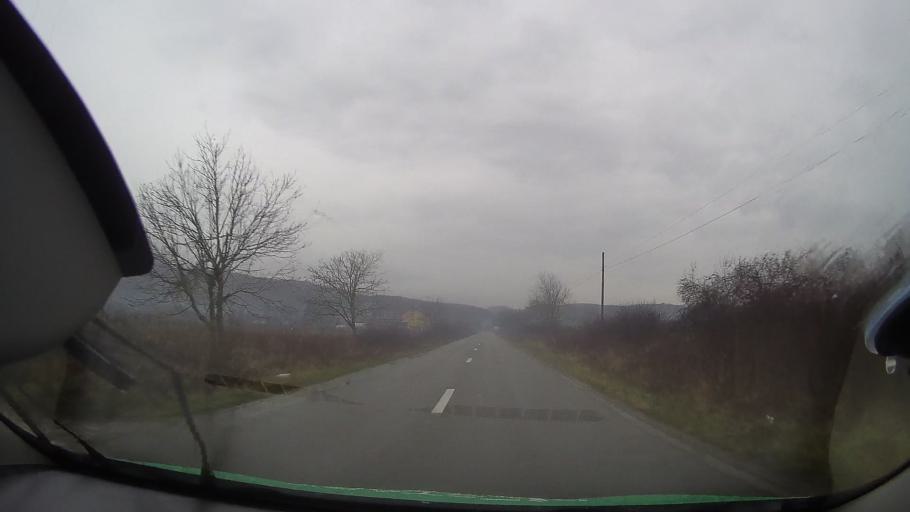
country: RO
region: Bihor
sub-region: Comuna Uileacu de Beius
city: Uileacu de Beius
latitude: 46.6801
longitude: 22.2318
